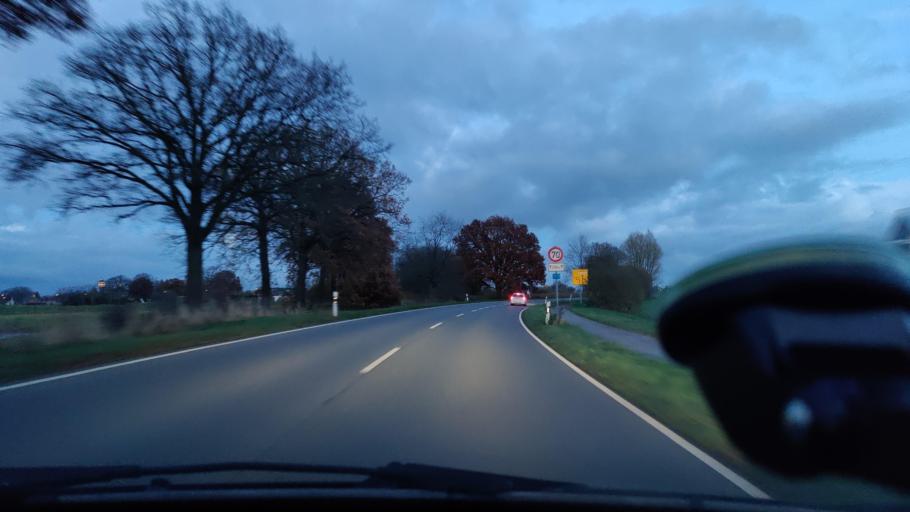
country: DE
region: North Rhine-Westphalia
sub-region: Regierungsbezirk Dusseldorf
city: Kevelaer
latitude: 51.5760
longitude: 6.2187
